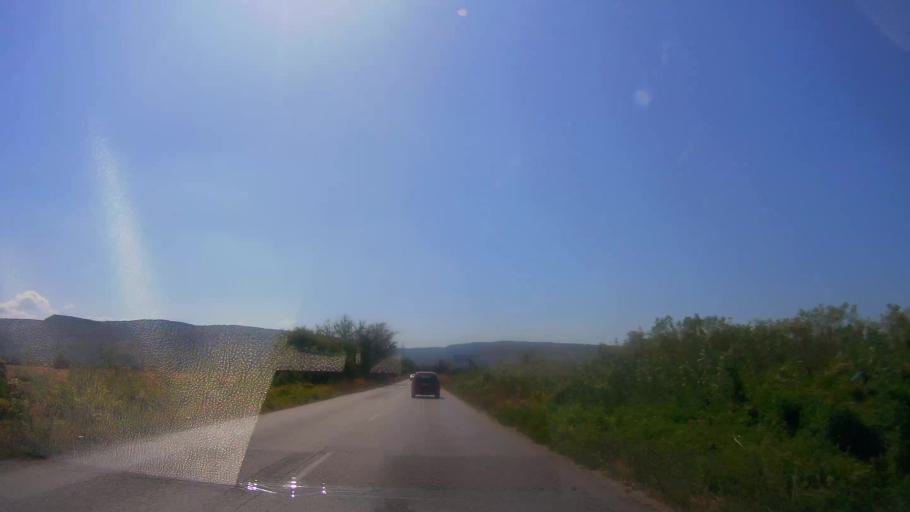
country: BG
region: Veliko Turnovo
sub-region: Obshtina Gorna Oryakhovitsa
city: Purvomaytsi
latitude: 43.1562
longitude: 25.6189
